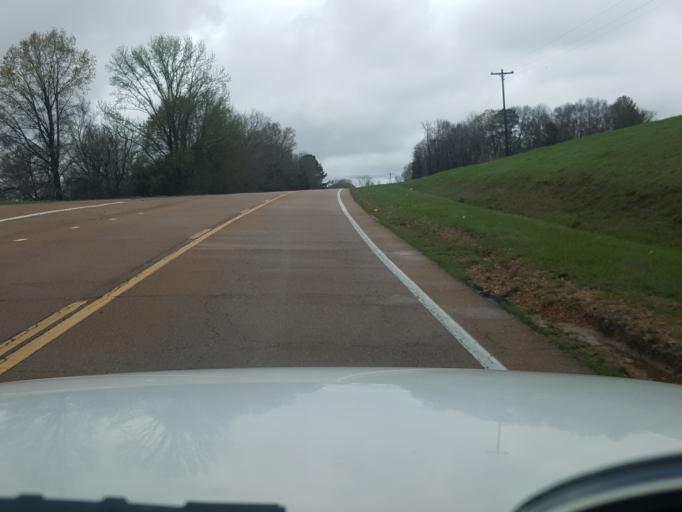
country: US
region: Mississippi
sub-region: Madison County
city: Canton
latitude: 32.7444
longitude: -90.1373
